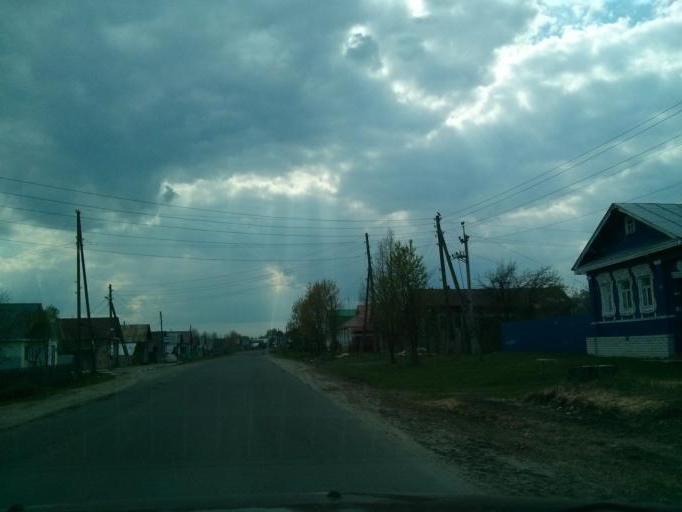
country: RU
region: Vladimir
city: Melenki
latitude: 55.3381
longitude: 41.8099
